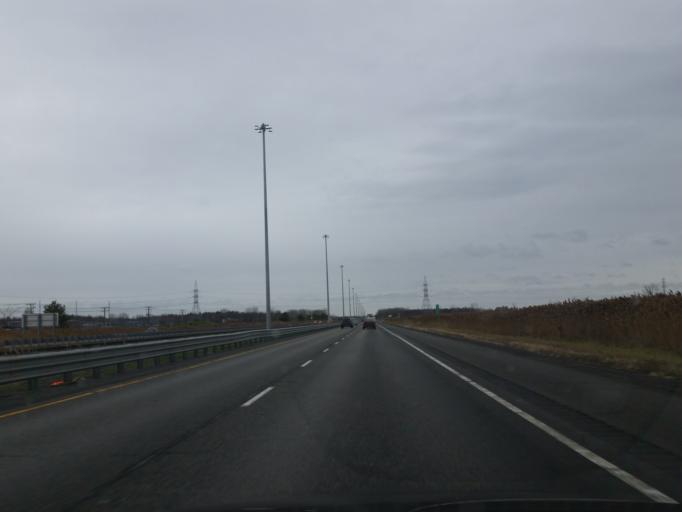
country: CA
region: Quebec
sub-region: Lanaudiere
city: Mascouche
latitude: 45.7212
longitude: -73.5468
